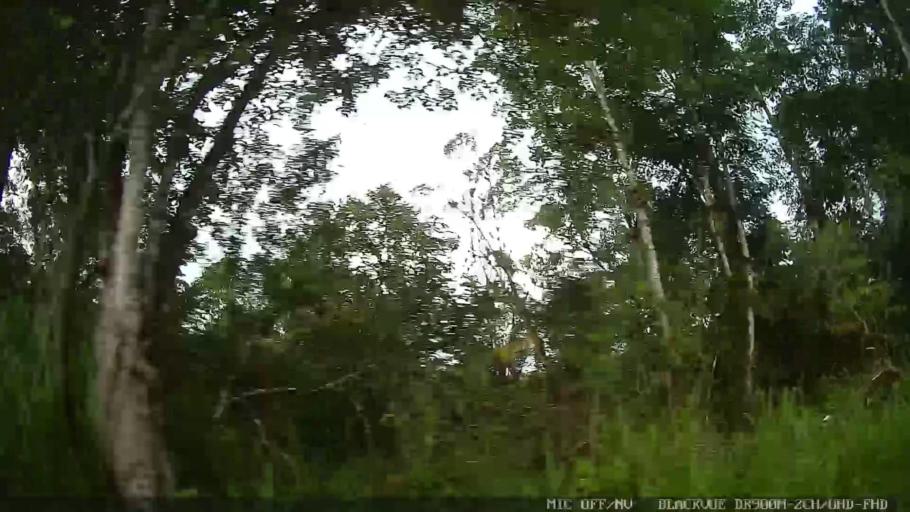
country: BR
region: Sao Paulo
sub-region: Itanhaem
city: Itanhaem
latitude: -24.0994
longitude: -46.8024
